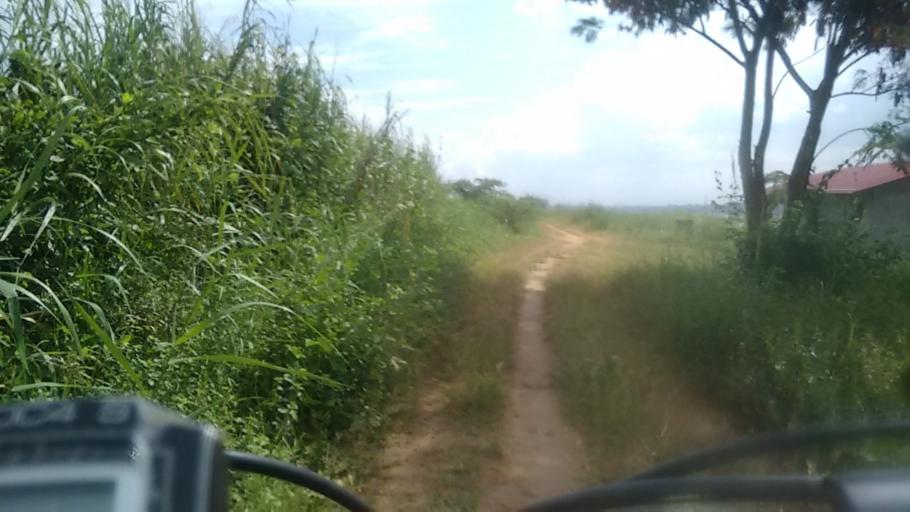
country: IN
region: Kerala
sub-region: Thrissur District
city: Trichur
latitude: 10.5305
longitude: 76.1487
